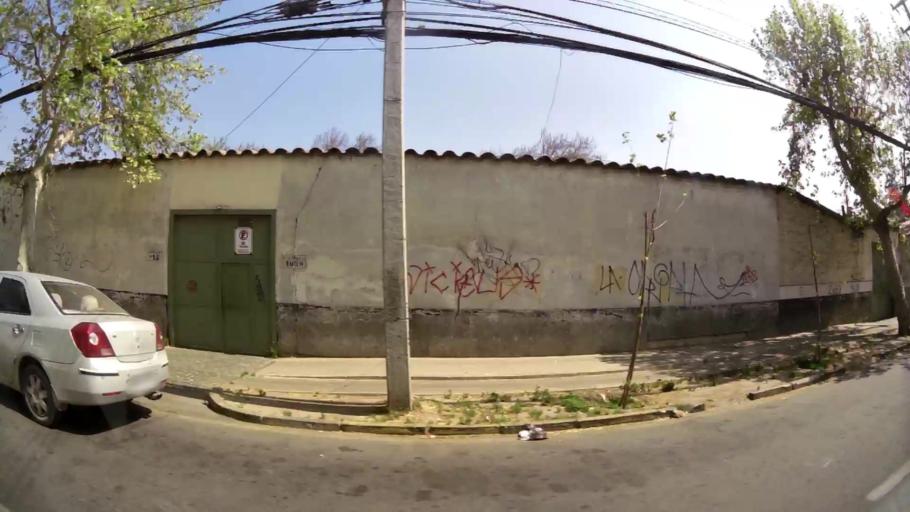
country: CL
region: Santiago Metropolitan
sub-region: Provincia de Santiago
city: Santiago
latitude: -33.4609
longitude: -70.6650
